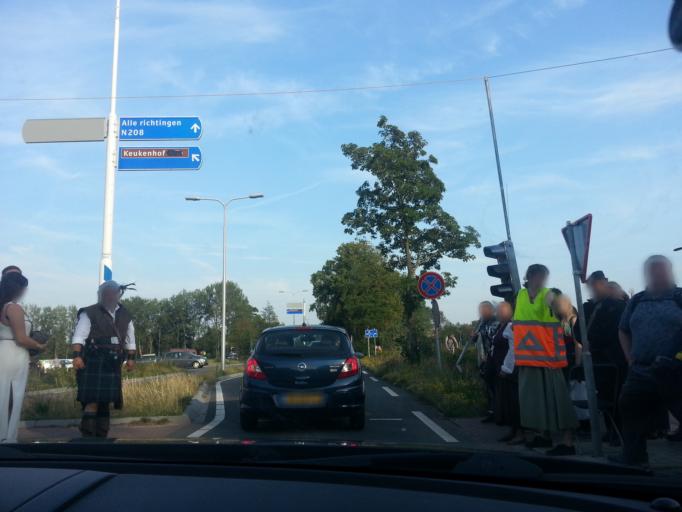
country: NL
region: South Holland
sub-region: Gemeente Lisse
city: Lisse
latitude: 52.2656
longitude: 4.5476
